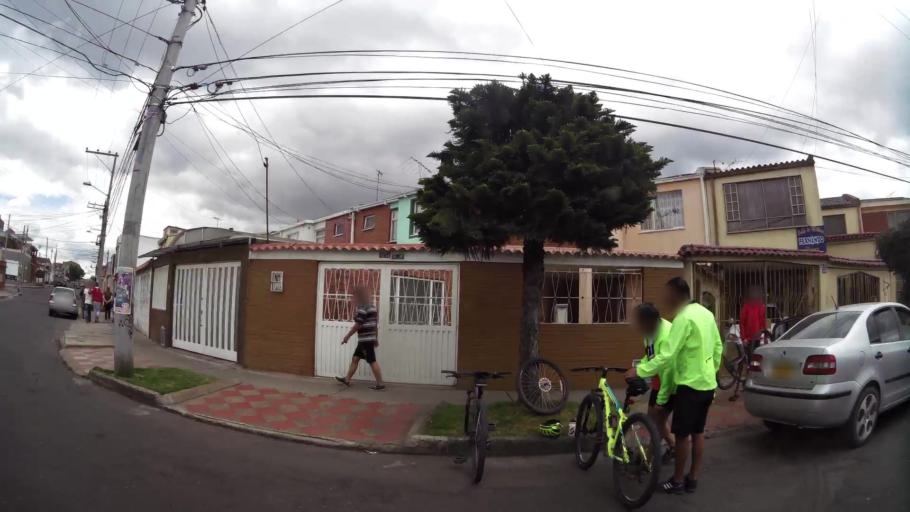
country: CO
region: Bogota D.C.
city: Bogota
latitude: 4.6129
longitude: -74.1257
